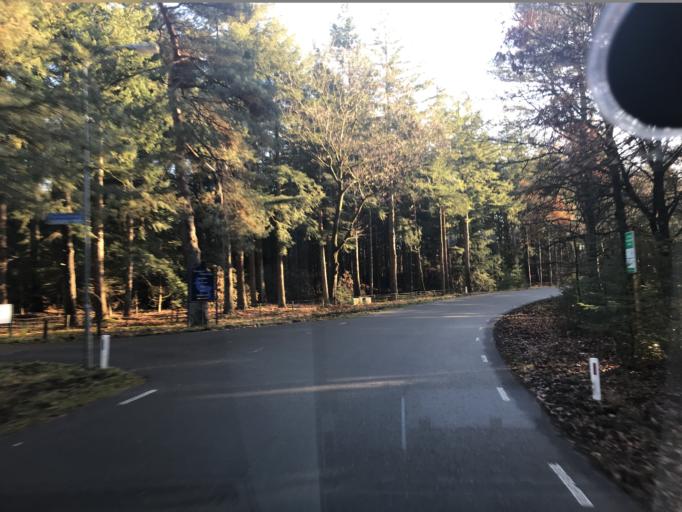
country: NL
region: Gelderland
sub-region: Gemeente Apeldoorn
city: Uddel
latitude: 52.3103
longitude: 5.7487
